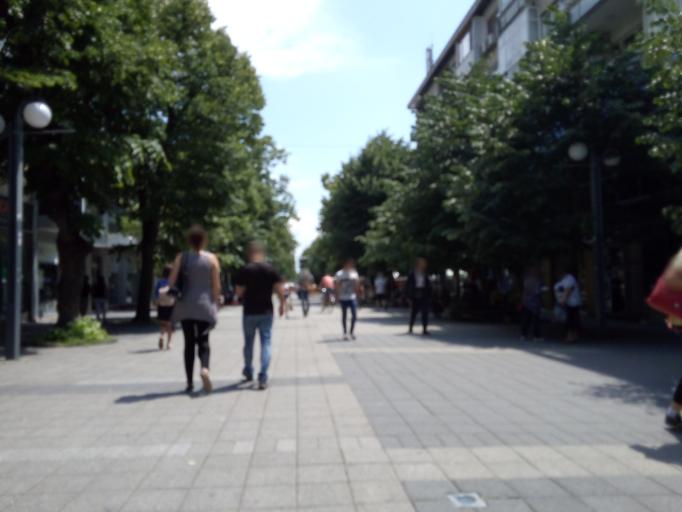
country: BG
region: Burgas
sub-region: Obshtina Burgas
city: Burgas
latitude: 42.4961
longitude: 27.4711
